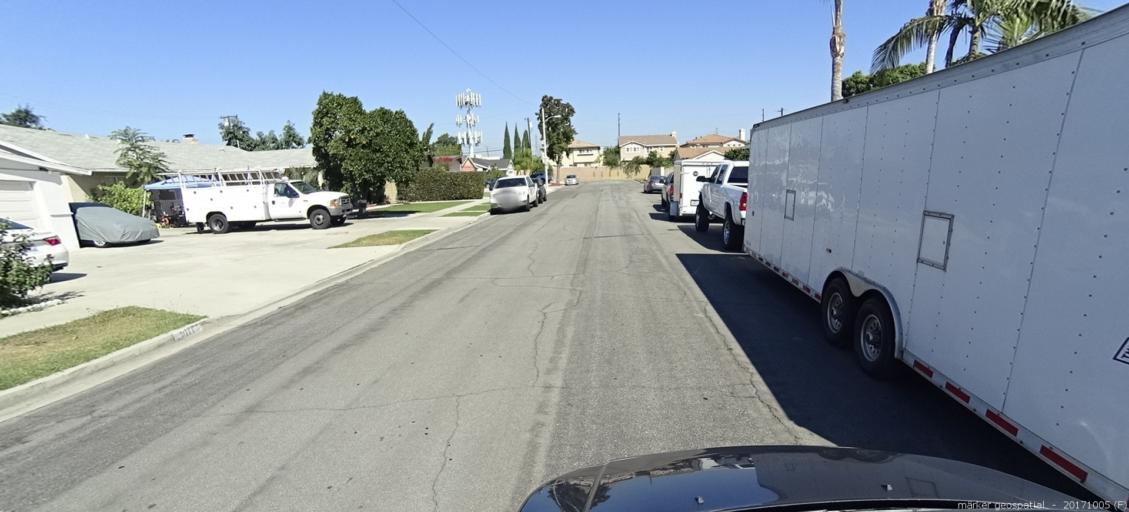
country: US
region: California
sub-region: Orange County
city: Stanton
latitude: 33.8014
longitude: -117.9714
